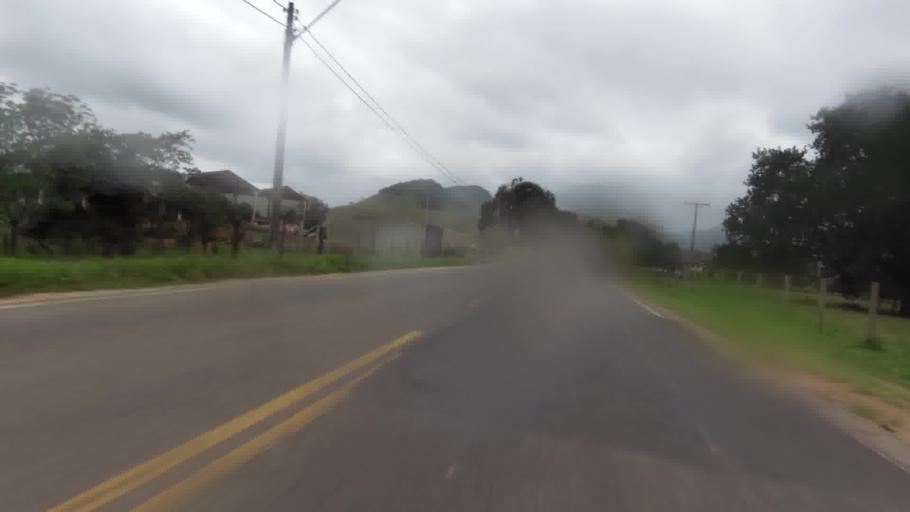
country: BR
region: Espirito Santo
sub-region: Alfredo Chaves
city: Alfredo Chaves
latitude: -20.6506
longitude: -40.7507
